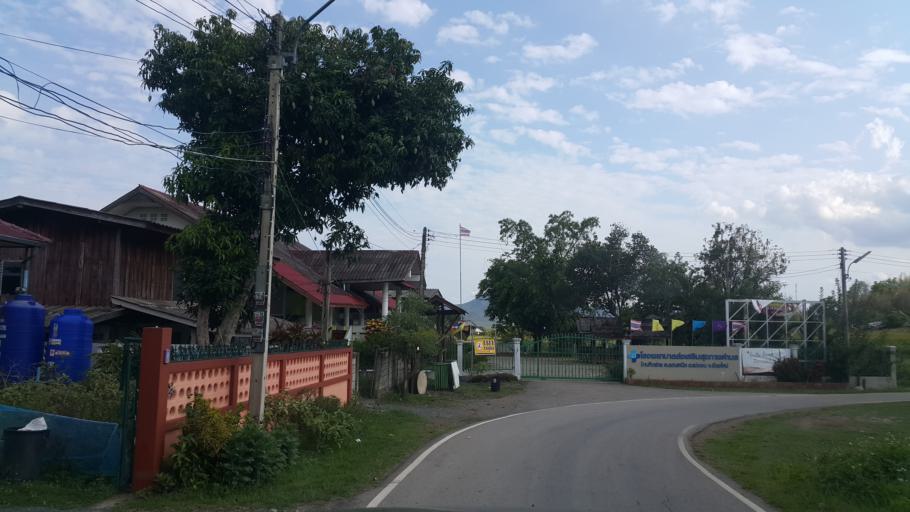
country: TH
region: Chiang Mai
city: Mae On
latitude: 18.7968
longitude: 99.2560
